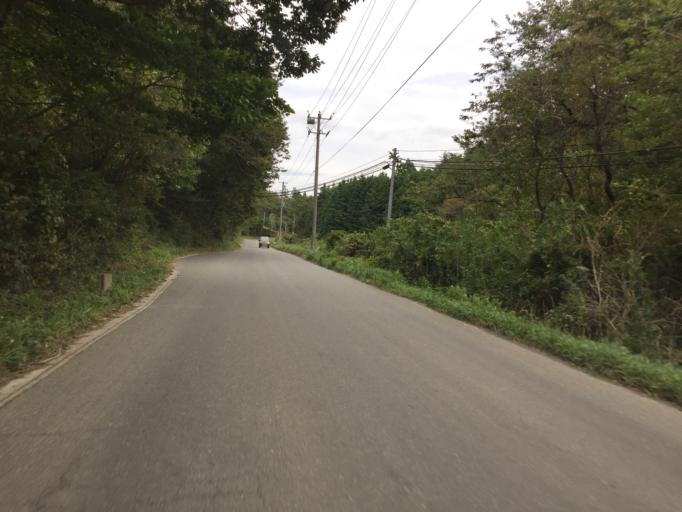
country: JP
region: Miyagi
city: Marumori
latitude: 37.8995
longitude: 140.7255
